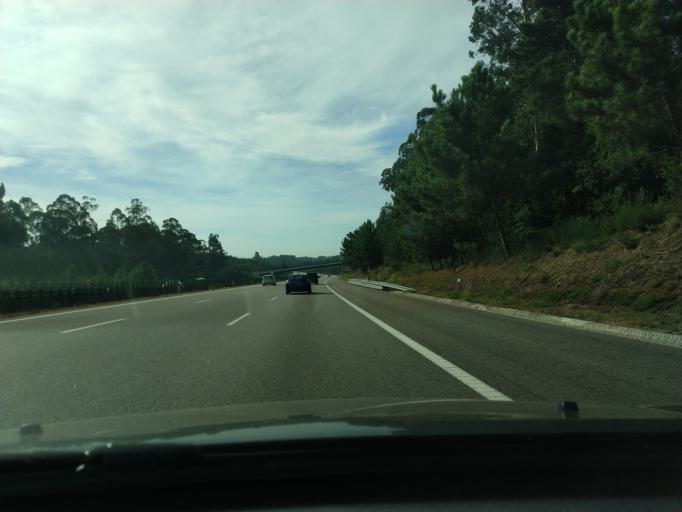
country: PT
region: Aveiro
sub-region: Santa Maria da Feira
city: Feira
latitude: 40.9022
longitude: -8.5671
